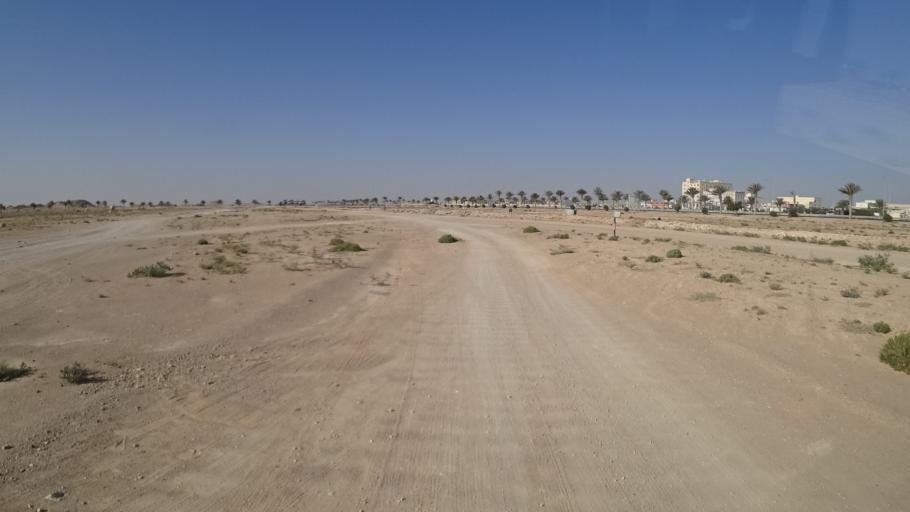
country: OM
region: Zufar
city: Salalah
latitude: 17.6080
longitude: 54.0324
